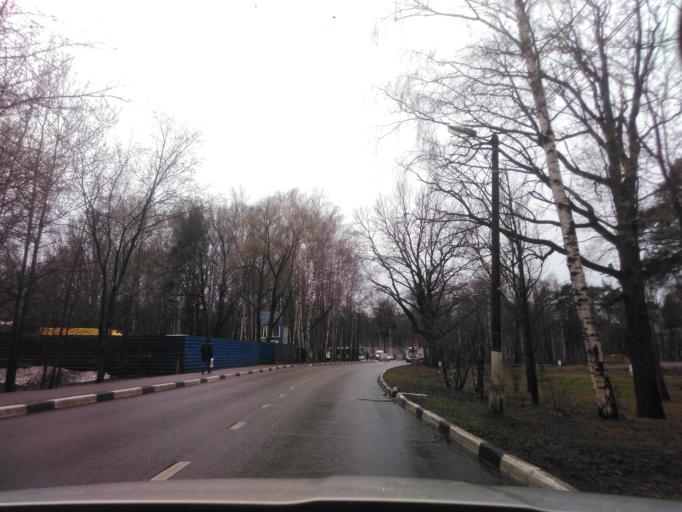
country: RU
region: Moskovskaya
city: Levoberezhnaya
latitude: 55.8892
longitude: 37.4690
